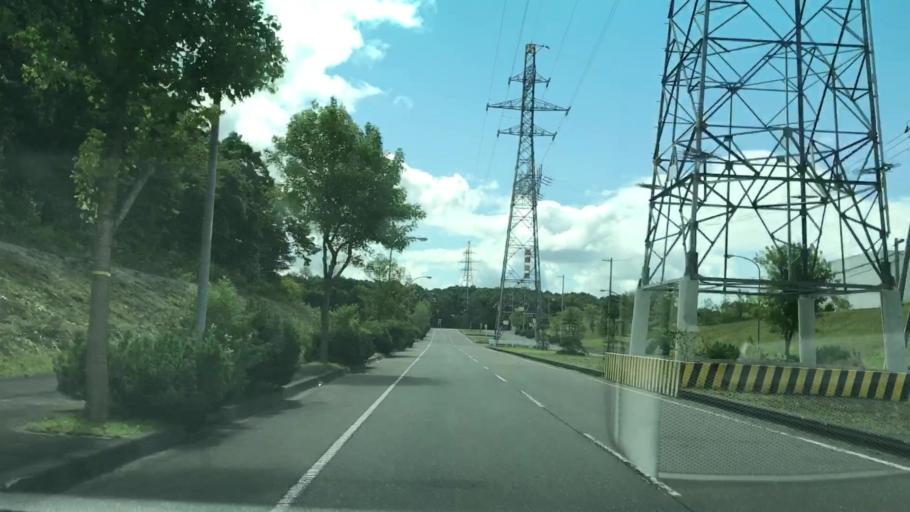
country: JP
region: Hokkaido
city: Chitose
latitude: 42.7751
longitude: 141.6166
